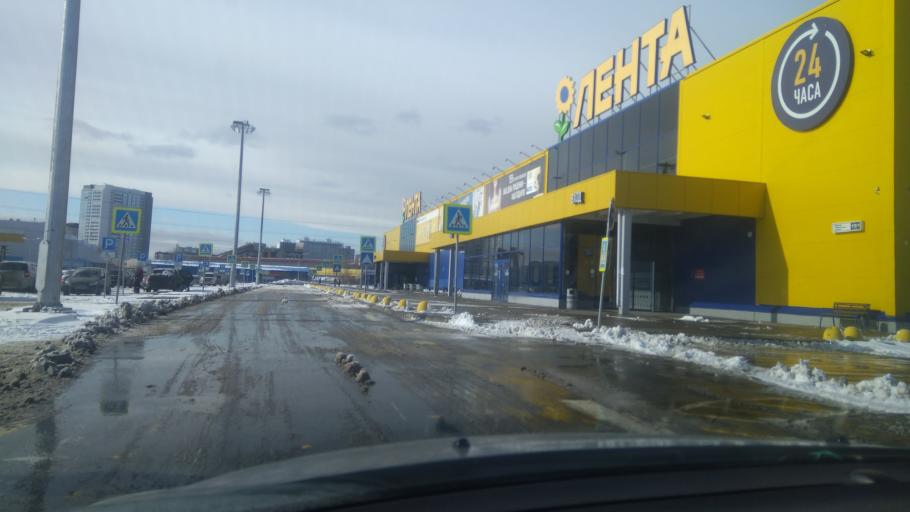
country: RU
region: Sverdlovsk
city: Istok
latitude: 56.8241
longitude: 60.7101
